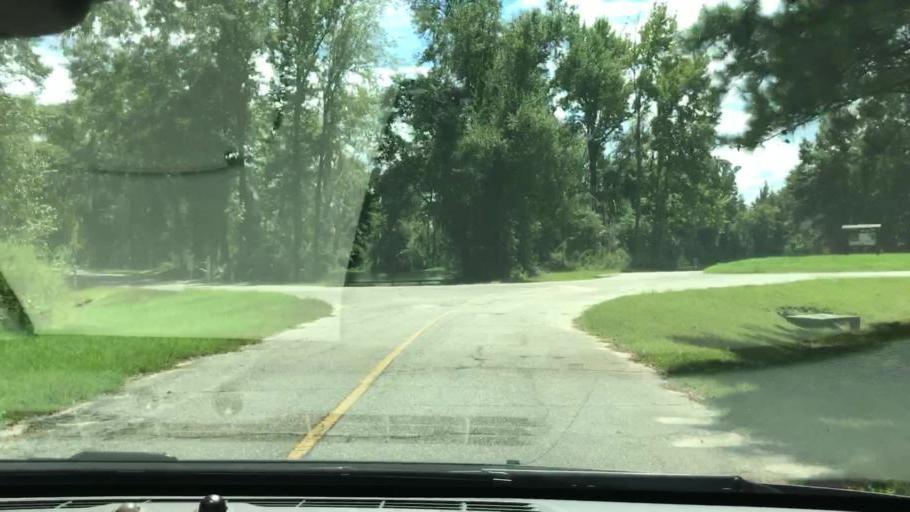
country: US
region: Georgia
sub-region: Quitman County
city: Georgetown
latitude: 32.0253
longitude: -85.0371
